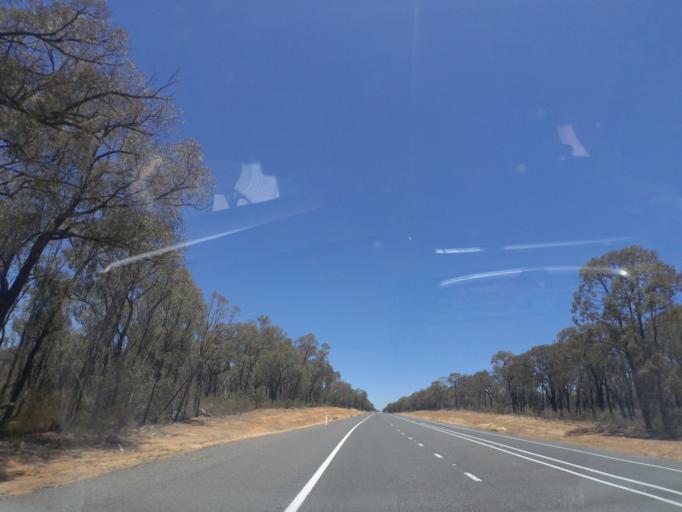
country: AU
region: New South Wales
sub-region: Warrumbungle Shire
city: Coonabarabran
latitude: -30.8941
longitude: 149.4415
